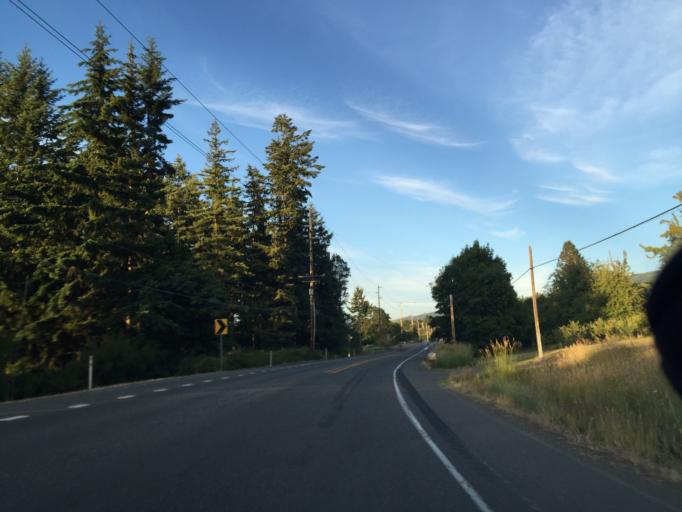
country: US
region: Washington
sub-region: Whatcom County
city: Geneva
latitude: 48.8041
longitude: -122.3961
